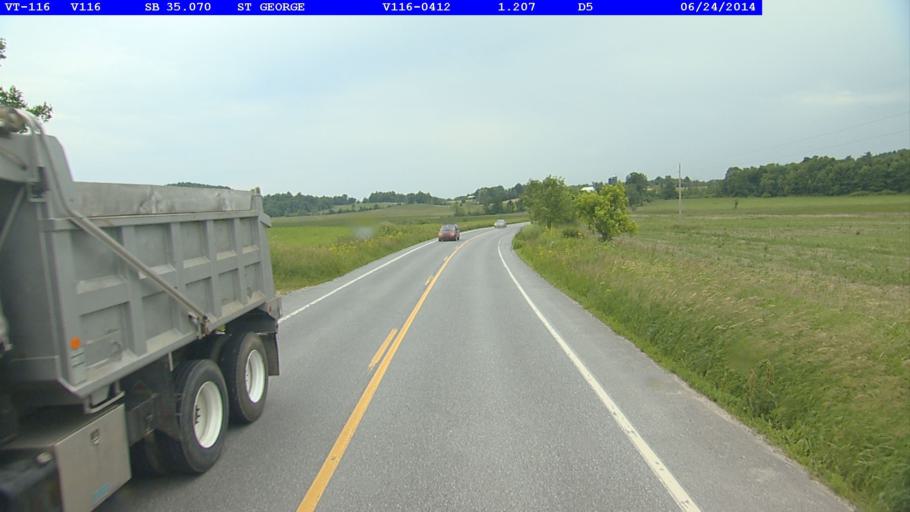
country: US
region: Vermont
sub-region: Chittenden County
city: Hinesburg
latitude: 44.3952
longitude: -73.1400
